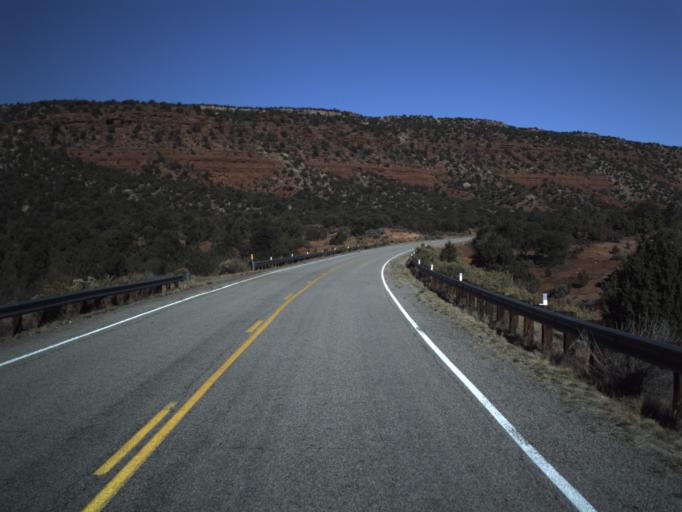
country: US
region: Utah
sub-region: San Juan County
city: Blanding
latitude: 37.5681
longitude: -110.0338
